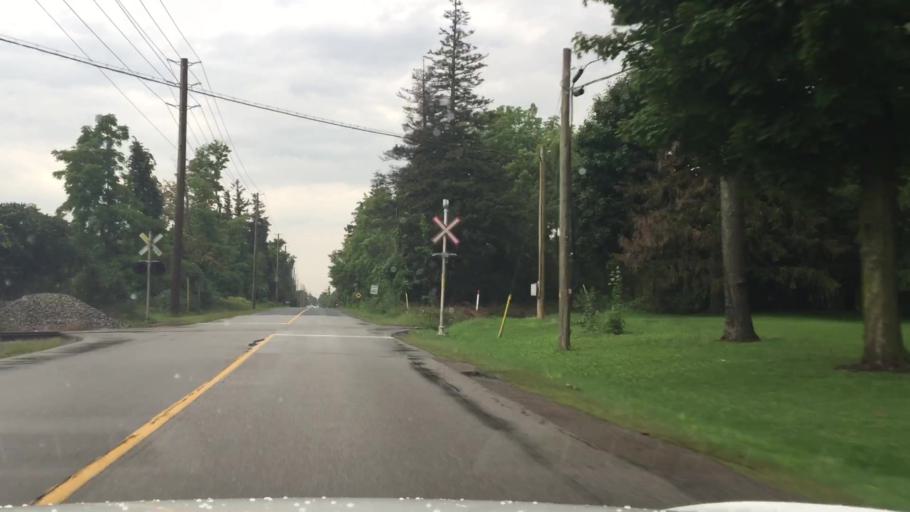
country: CA
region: Ontario
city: Markham
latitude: 43.8724
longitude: -79.2076
